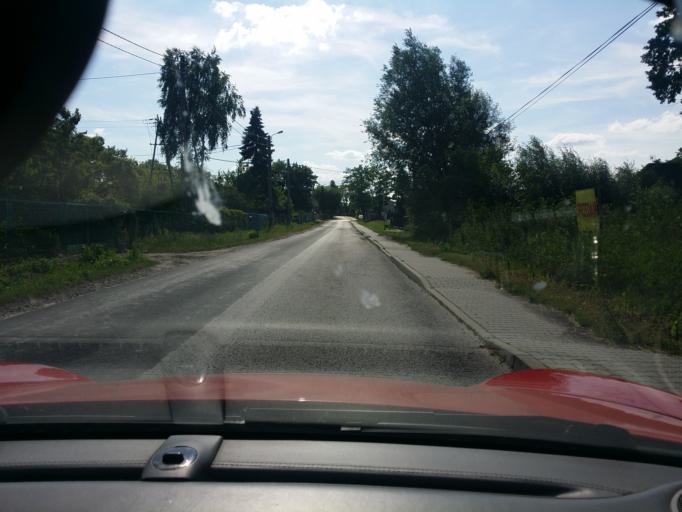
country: PL
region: Masovian Voivodeship
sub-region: Powiat radomski
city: Trablice
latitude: 51.3498
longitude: 21.1142
